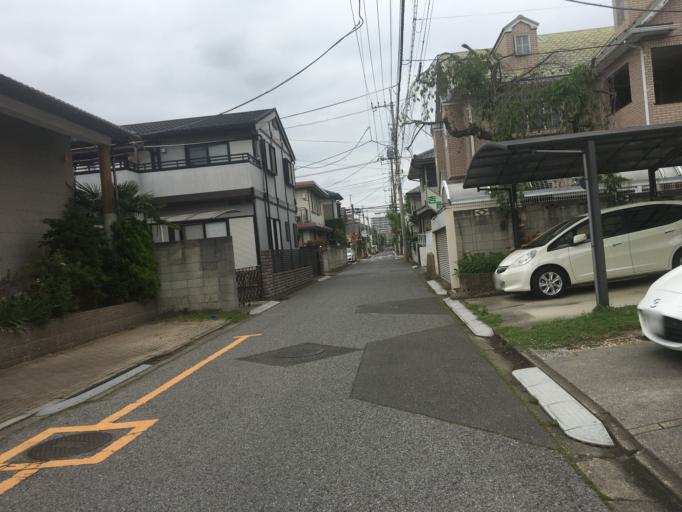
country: JP
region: Saitama
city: Yono
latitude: 35.8578
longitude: 139.6426
